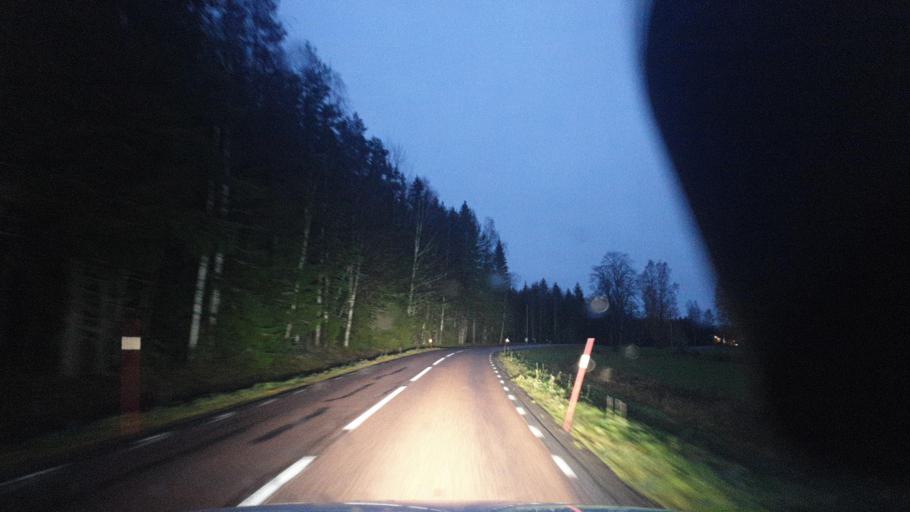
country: SE
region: Vaermland
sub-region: Eda Kommun
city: Amotfors
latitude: 59.7492
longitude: 12.2118
